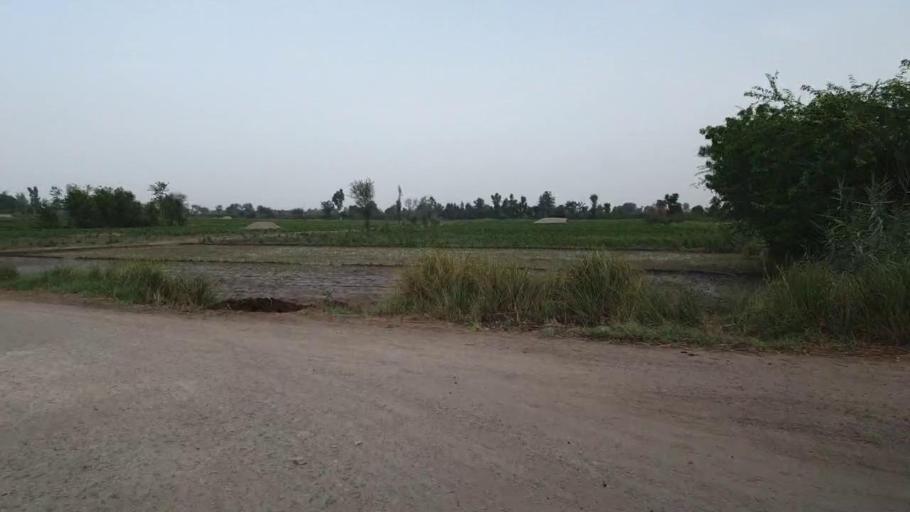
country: PK
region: Sindh
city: Bandhi
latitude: 26.5320
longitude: 68.2043
